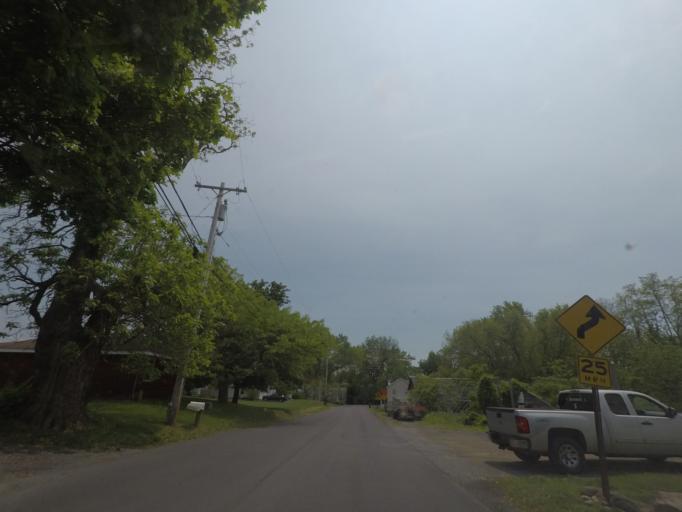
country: US
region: New York
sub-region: Rensselaer County
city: Castleton-on-Hudson
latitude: 42.5122
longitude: -73.7058
